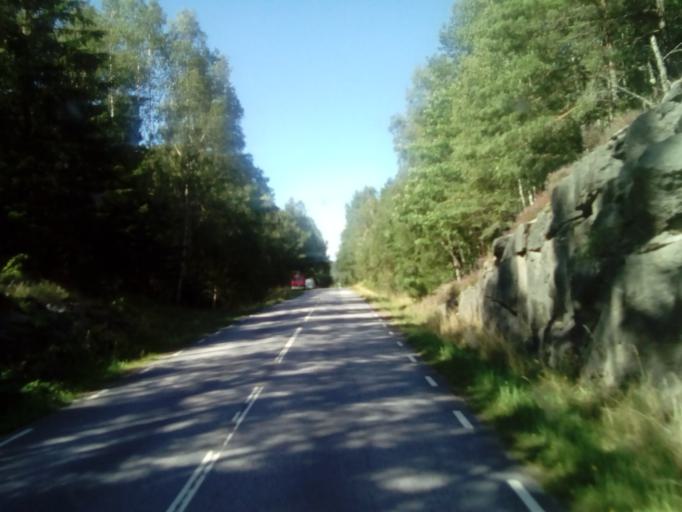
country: SE
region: Kalmar
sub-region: Vimmerby Kommun
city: Sodra Vi
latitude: 57.9090
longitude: 15.9915
